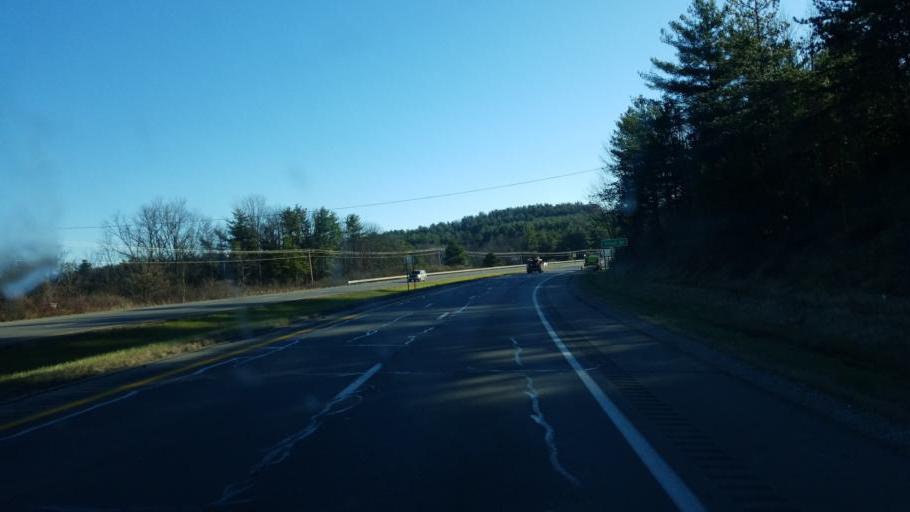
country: US
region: Ohio
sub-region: Richland County
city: Lincoln Heights
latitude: 40.7870
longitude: -82.3942
